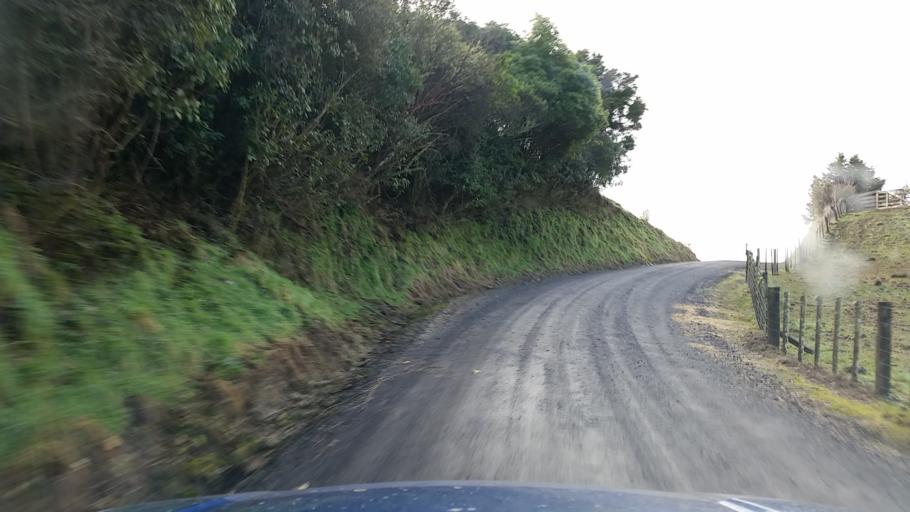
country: NZ
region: Taranaki
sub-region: New Plymouth District
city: Waitara
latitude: -39.0727
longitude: 174.7982
